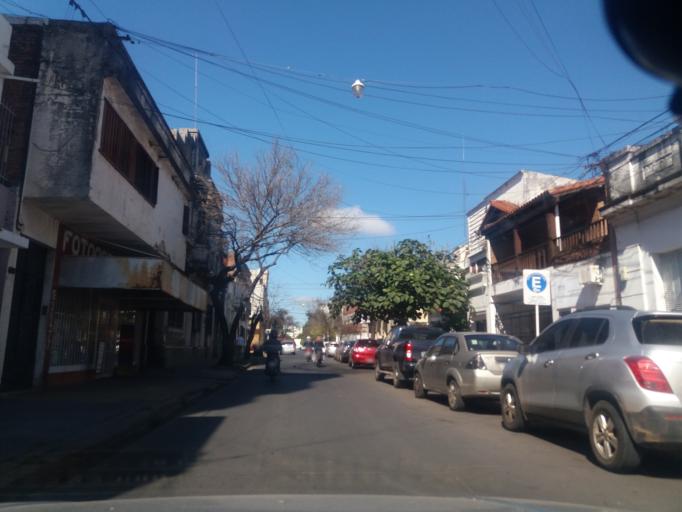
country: AR
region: Corrientes
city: Corrientes
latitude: -27.4728
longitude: -58.8350
